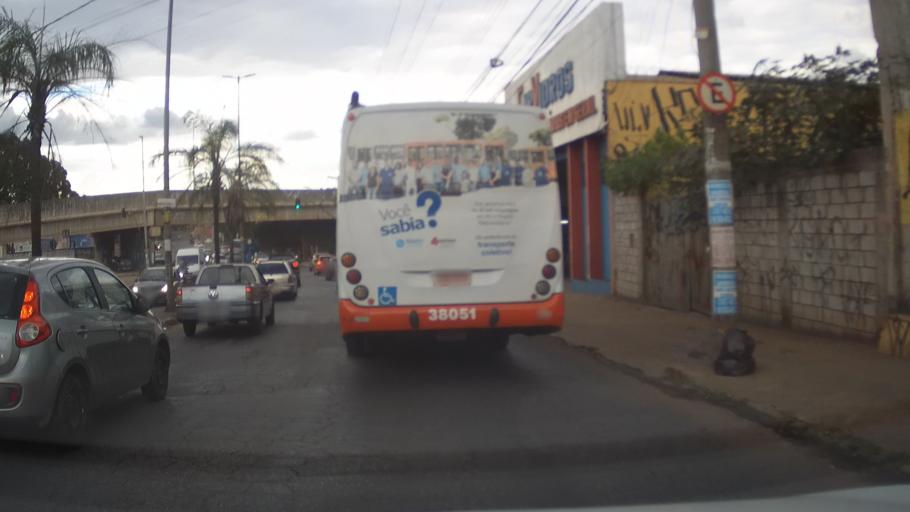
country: BR
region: Minas Gerais
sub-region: Contagem
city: Contagem
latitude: -19.9576
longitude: -44.0161
